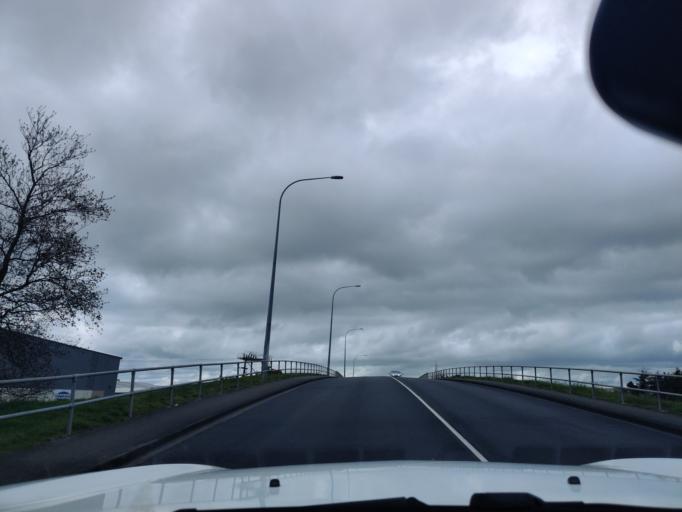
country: NZ
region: Manawatu-Wanganui
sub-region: Palmerston North City
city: Palmerston North
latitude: -40.3382
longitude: 175.6437
